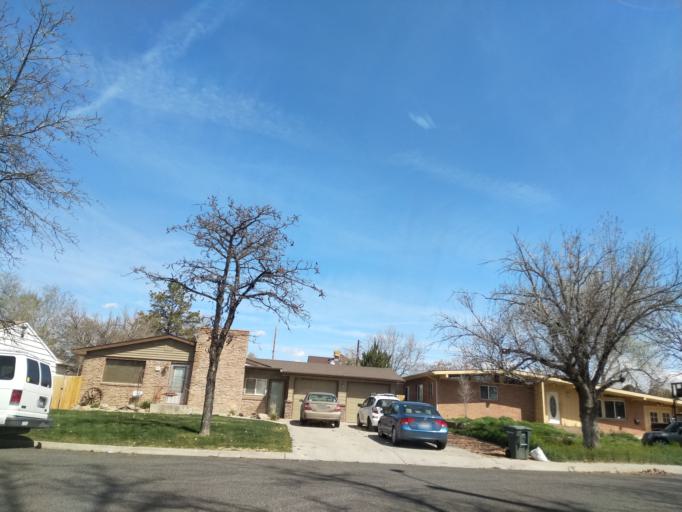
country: US
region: Colorado
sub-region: Mesa County
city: Grand Junction
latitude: 39.0836
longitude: -108.5454
